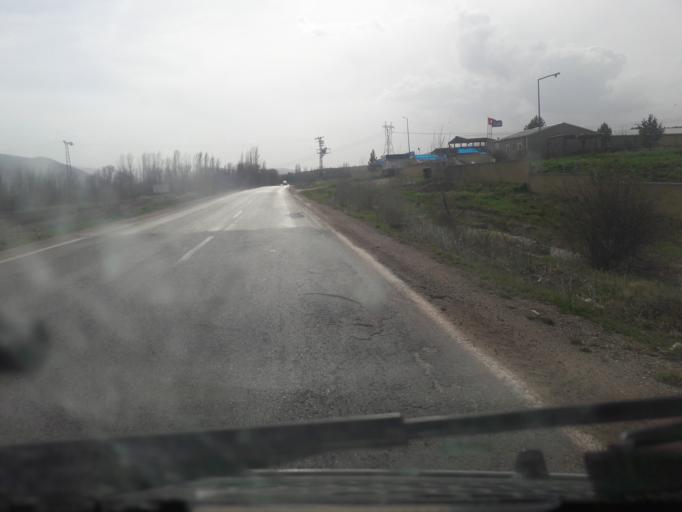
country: TR
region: Gumushane
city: Kelkit
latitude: 40.1309
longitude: 39.3668
